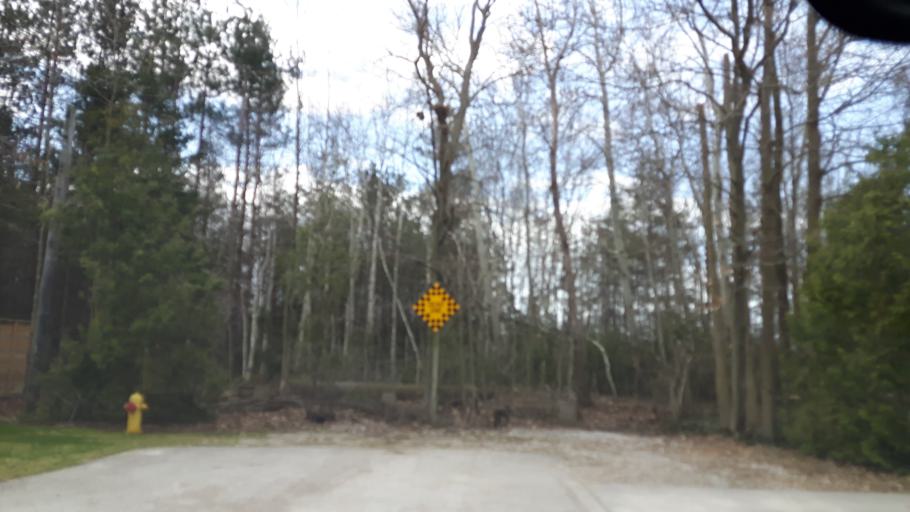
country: CA
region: Ontario
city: Bluewater
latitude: 43.5541
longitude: -81.6974
